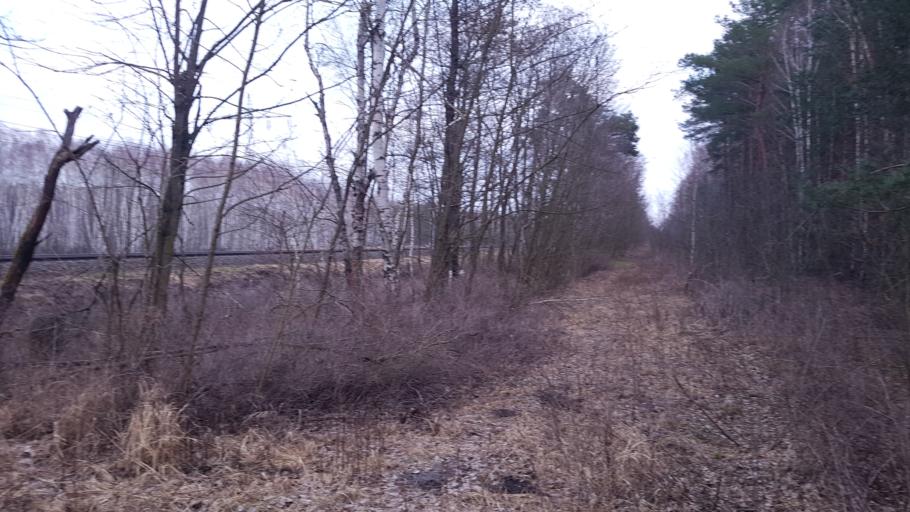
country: DE
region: Brandenburg
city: Trobitz
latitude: 51.5954
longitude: 13.4097
